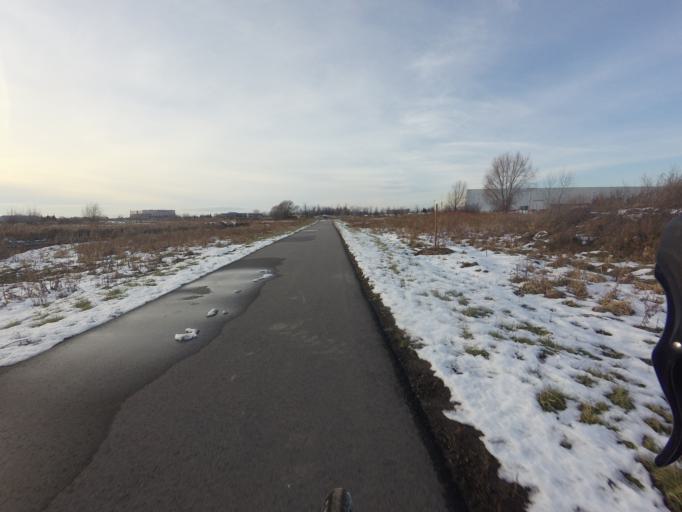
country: CA
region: Ontario
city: Bells Corners
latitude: 45.2960
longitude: -75.9108
